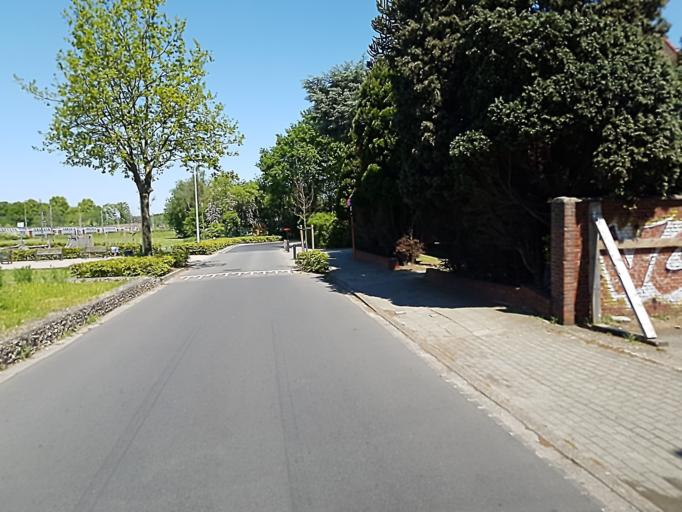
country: BE
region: Flanders
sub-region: Provincie Antwerpen
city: Turnhout
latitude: 51.3272
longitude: 4.9414
